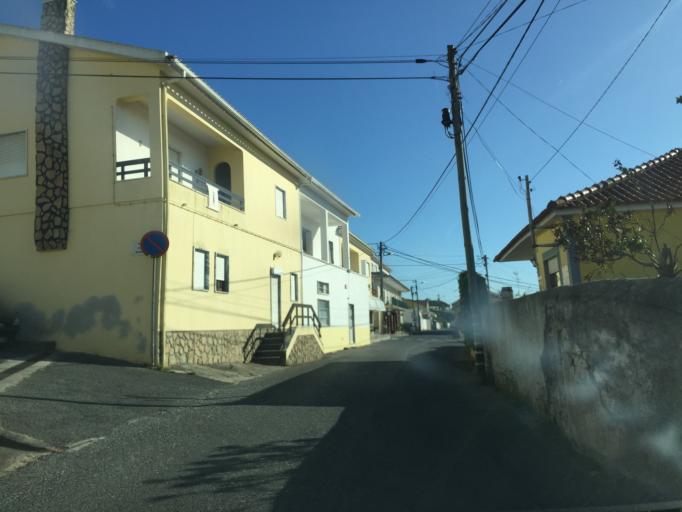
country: PT
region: Lisbon
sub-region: Torres Vedras
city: Torres Vedras
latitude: 39.0893
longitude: -9.2775
